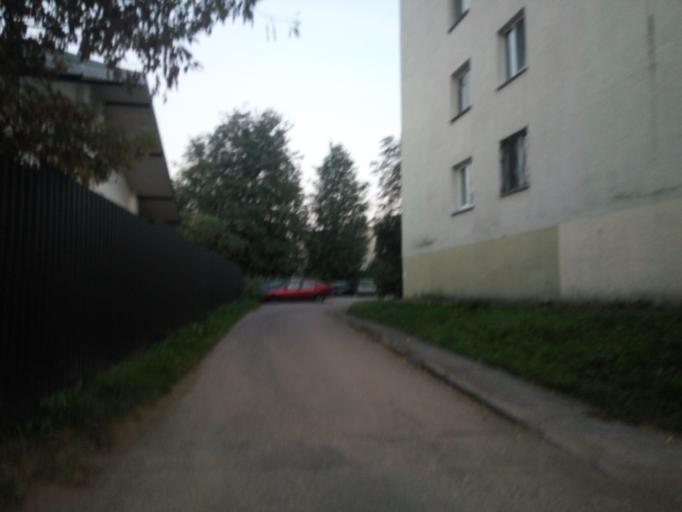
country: BY
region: Vitebsk
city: Vitebsk
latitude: 55.2019
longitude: 30.2425
